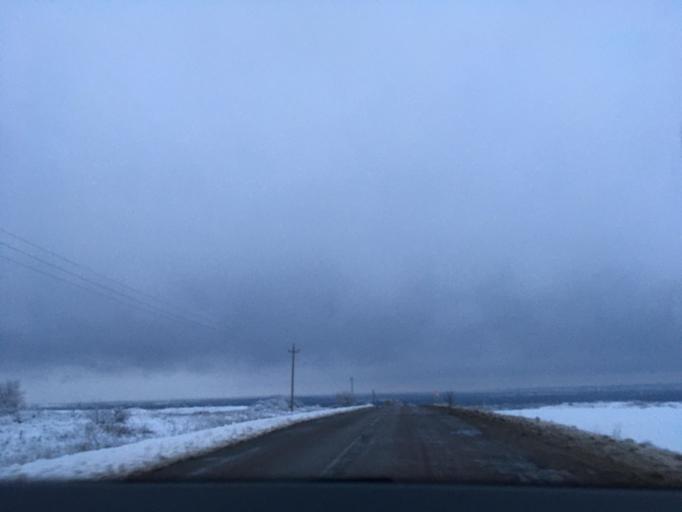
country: RU
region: Voronezj
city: Verkhniy Mamon
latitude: 50.0706
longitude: 40.2874
